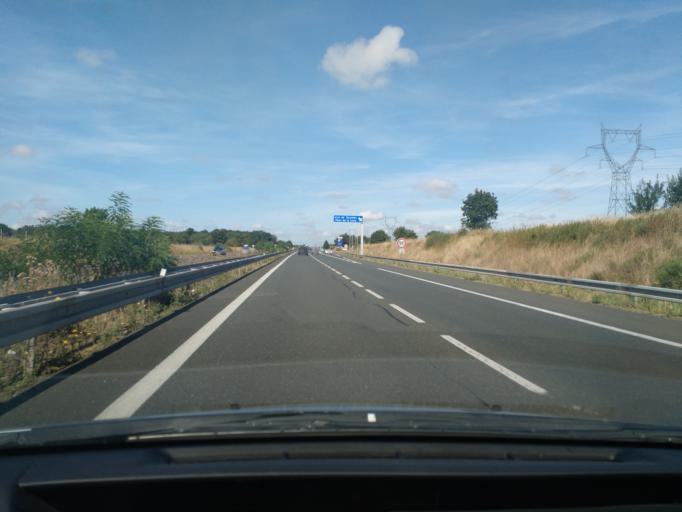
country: FR
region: Pays de la Loire
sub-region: Departement de la Loire-Atlantique
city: Varades
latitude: 47.4183
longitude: -1.0094
